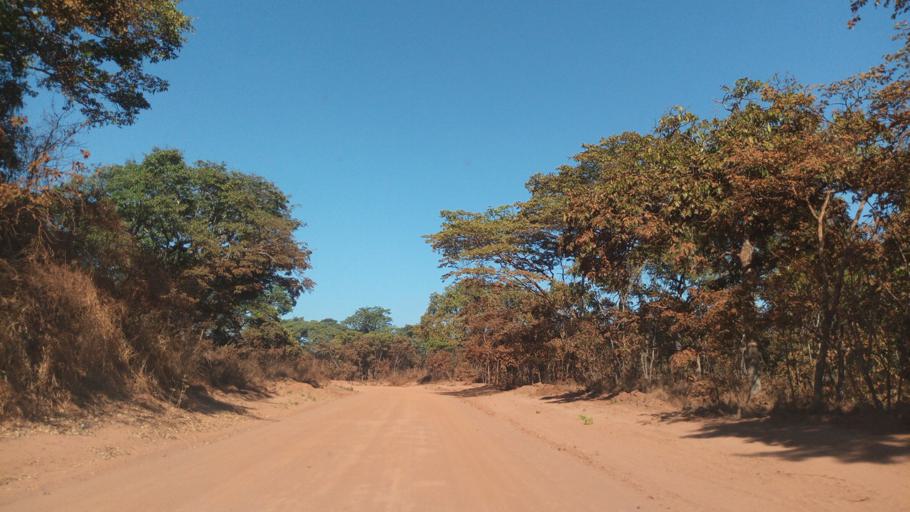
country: ZM
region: Luapula
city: Mwense
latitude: -10.7435
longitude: 28.3277
